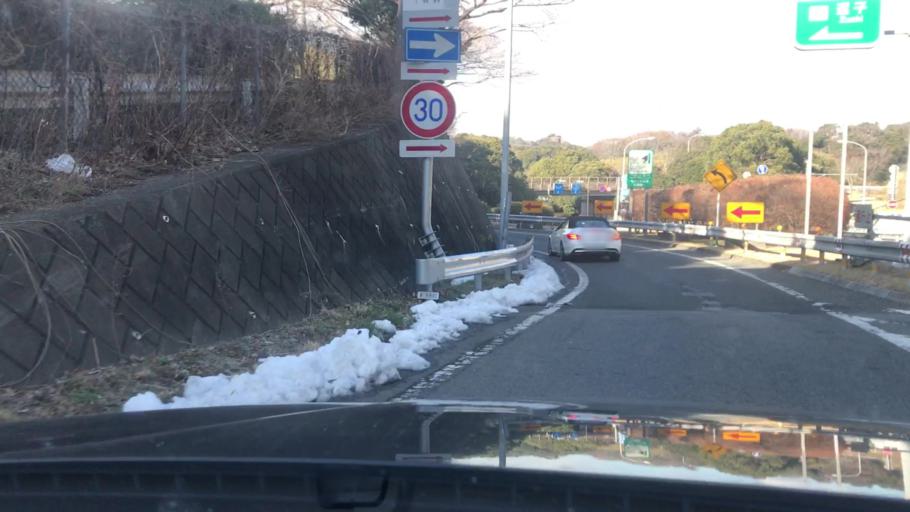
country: JP
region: Kanagawa
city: Zushi
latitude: 35.2937
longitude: 139.6132
